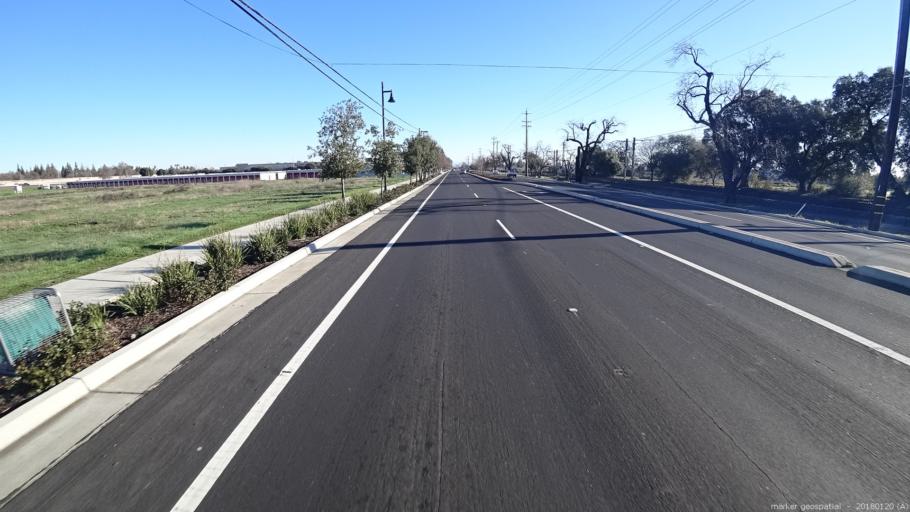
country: US
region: California
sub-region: Sacramento County
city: Rancho Cordova
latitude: 38.6028
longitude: -121.2753
